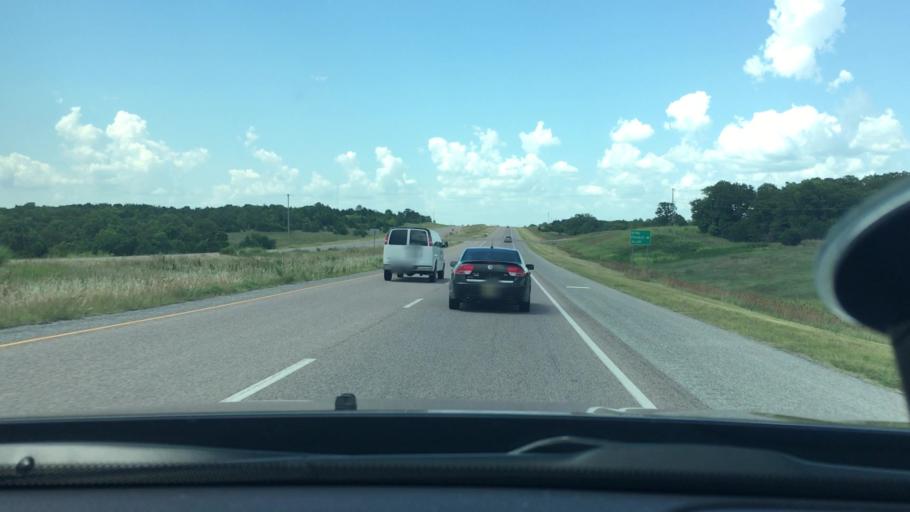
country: US
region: Oklahoma
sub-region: Pontotoc County
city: Byng
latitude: 34.8661
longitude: -96.6798
